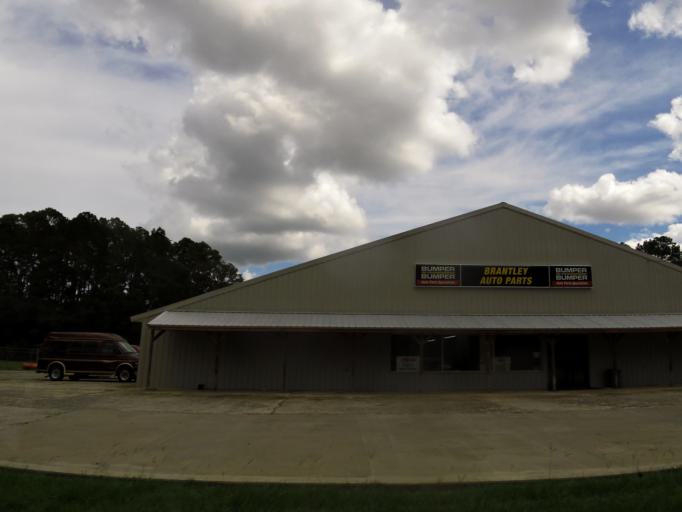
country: US
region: Georgia
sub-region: Brantley County
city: Nahunta
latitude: 31.2002
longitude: -81.9833
